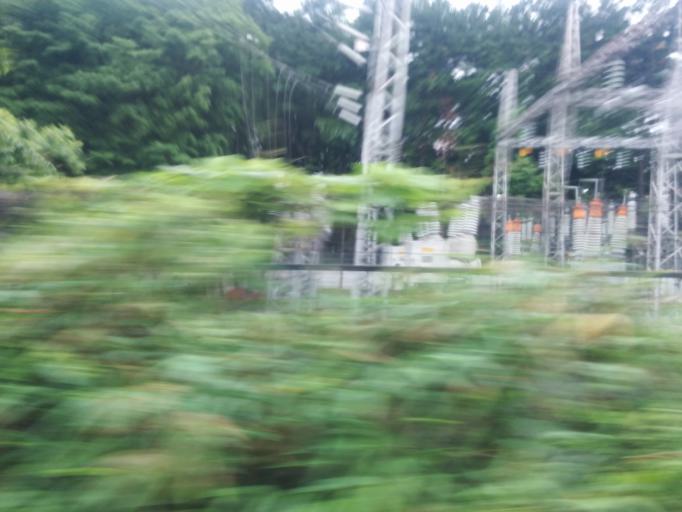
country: JP
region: Tochigi
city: Kanuma
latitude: 36.5973
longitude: 139.7485
